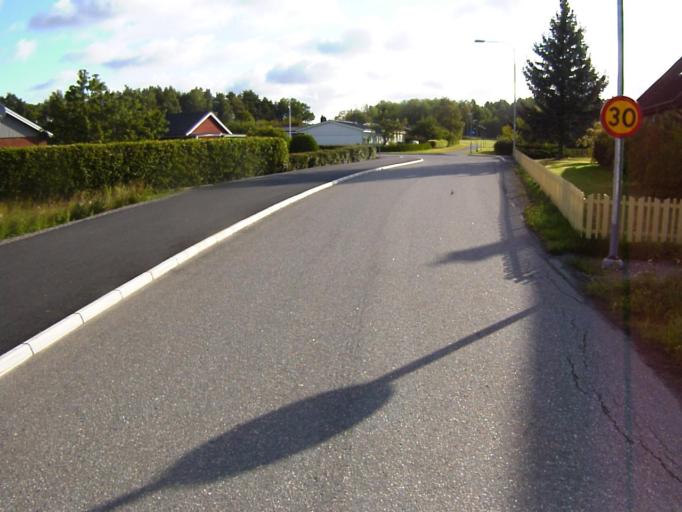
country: SE
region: Soedermanland
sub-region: Eskilstuna Kommun
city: Eskilstuna
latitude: 59.3749
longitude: 16.5478
